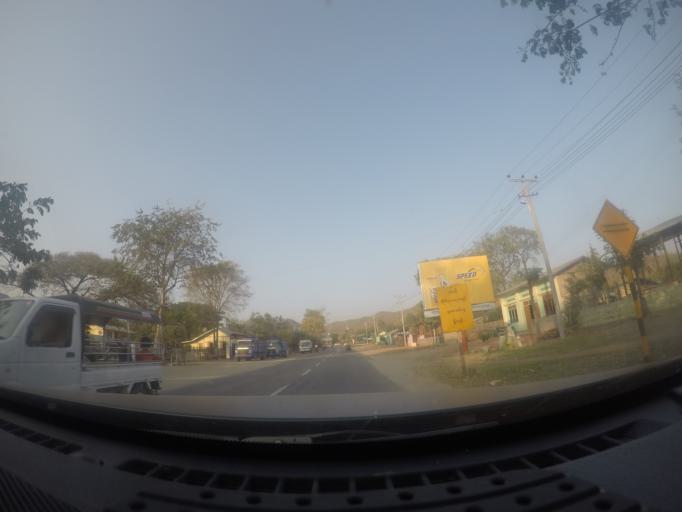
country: MM
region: Mandalay
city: Yamethin
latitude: 20.7442
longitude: 96.2154
